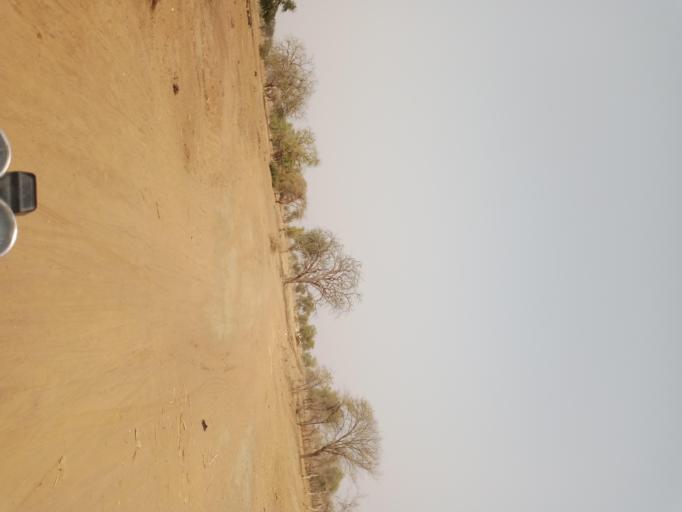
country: BF
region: Est
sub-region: Gnagna Province
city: Bogande
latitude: 13.2767
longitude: -0.1762
